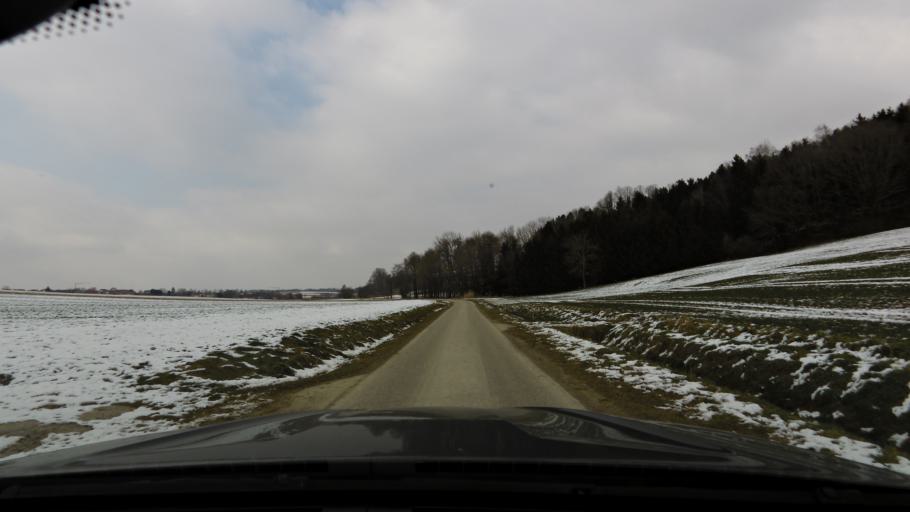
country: DE
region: Bavaria
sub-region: Lower Bavaria
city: Eching
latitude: 48.4660
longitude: 12.0517
